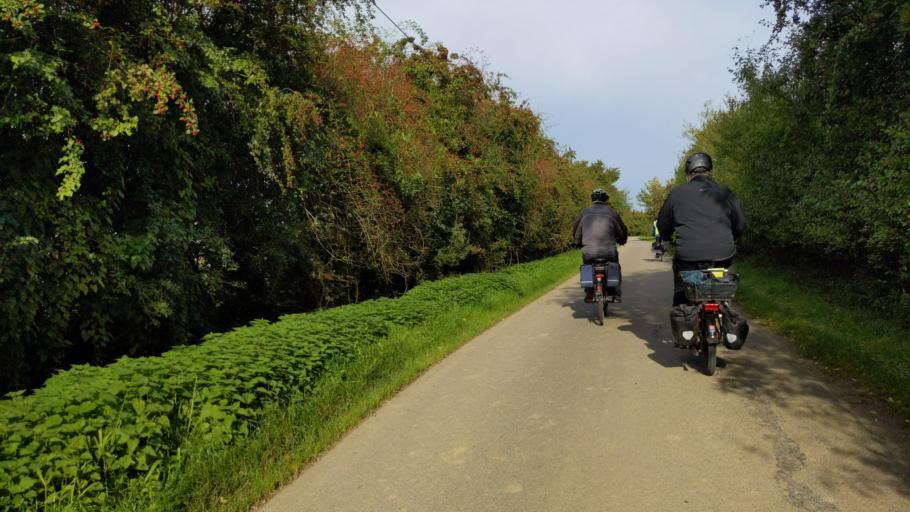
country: DE
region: Schleswig-Holstein
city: Zarpen
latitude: 53.8770
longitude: 10.5131
